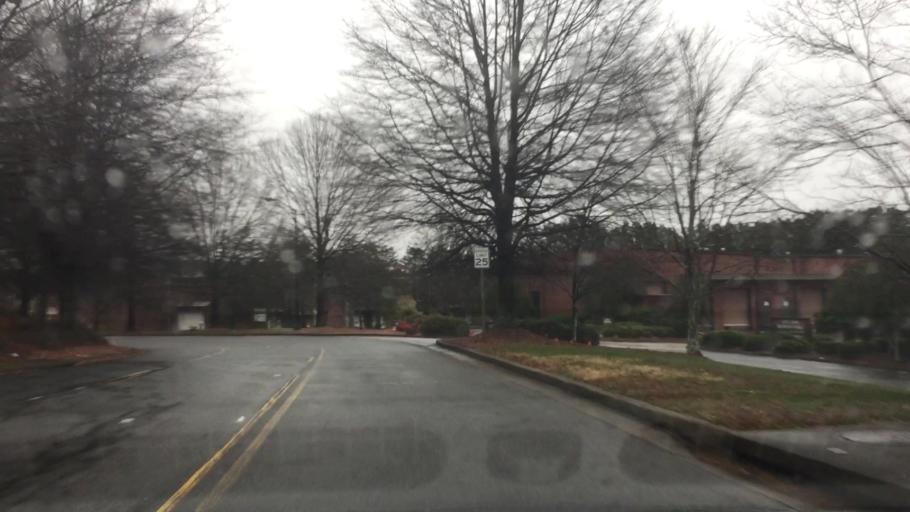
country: US
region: Georgia
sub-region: Cobb County
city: Marietta
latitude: 33.9814
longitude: -84.5239
